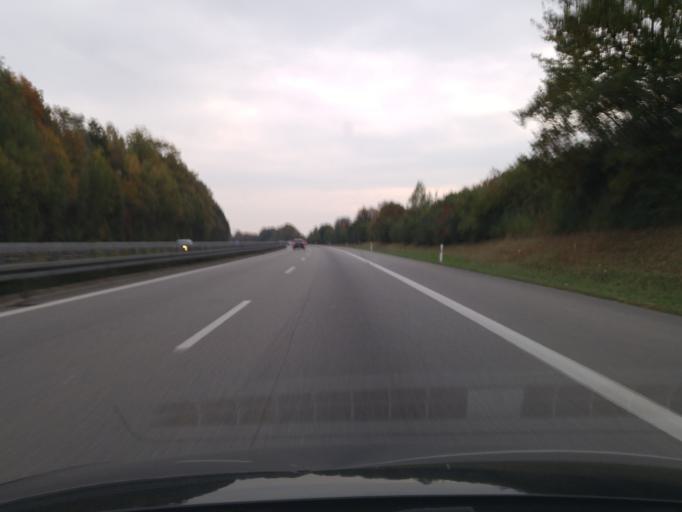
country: DE
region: Baden-Wuerttemberg
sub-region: Regierungsbezirk Stuttgart
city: Bretzfeld
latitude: 49.1739
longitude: 9.3903
